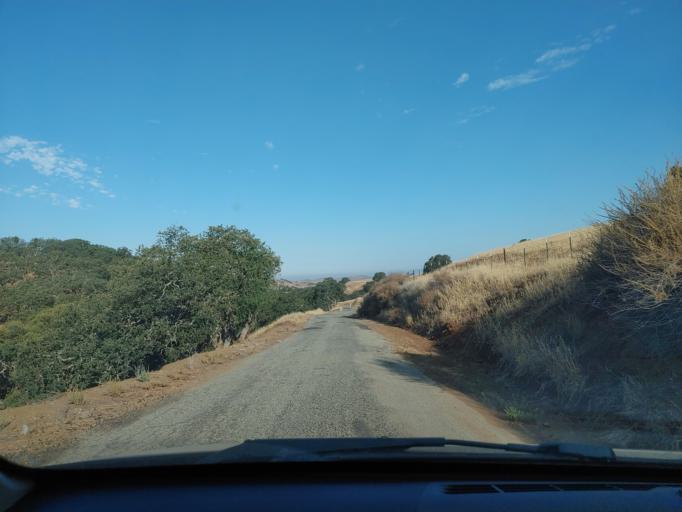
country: US
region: California
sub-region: San Benito County
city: Ridgemark
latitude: 36.7707
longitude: -121.2193
